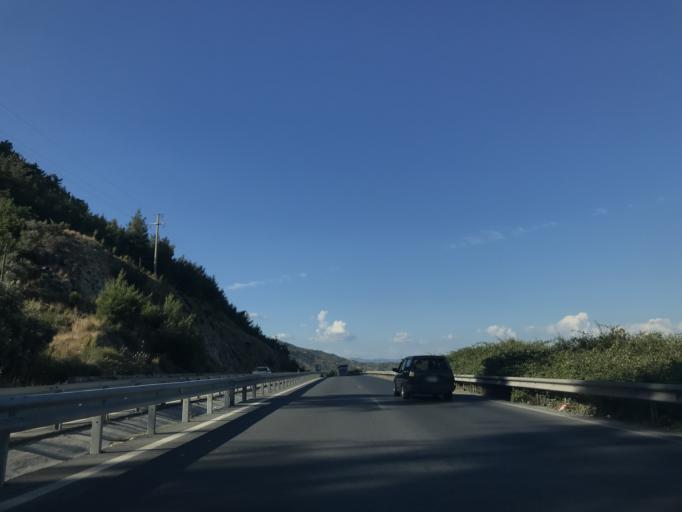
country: TR
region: Aydin
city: Ortaklar
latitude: 37.8054
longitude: 27.4778
